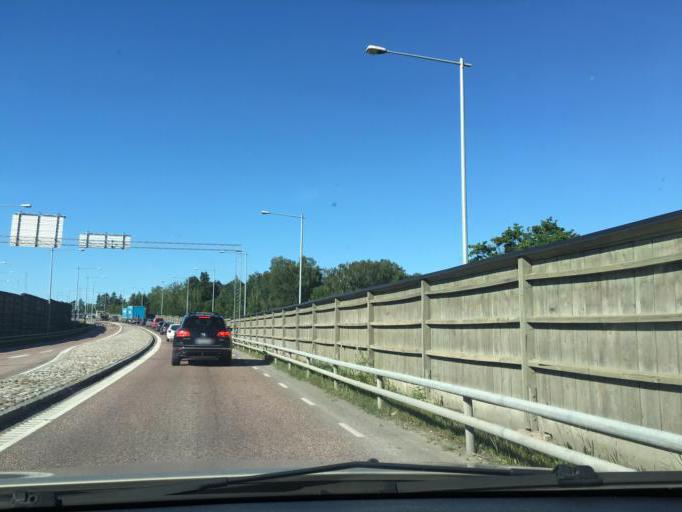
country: SE
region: Stockholm
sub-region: Sodertalje Kommun
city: Soedertaelje
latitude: 59.1884
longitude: 17.6453
